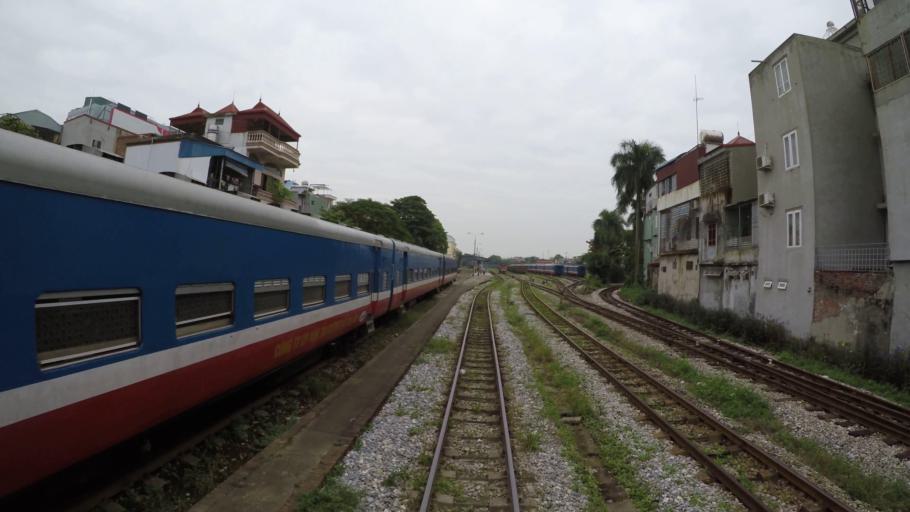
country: VN
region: Hai Phong
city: Haiphong
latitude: 20.8516
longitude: 106.6758
